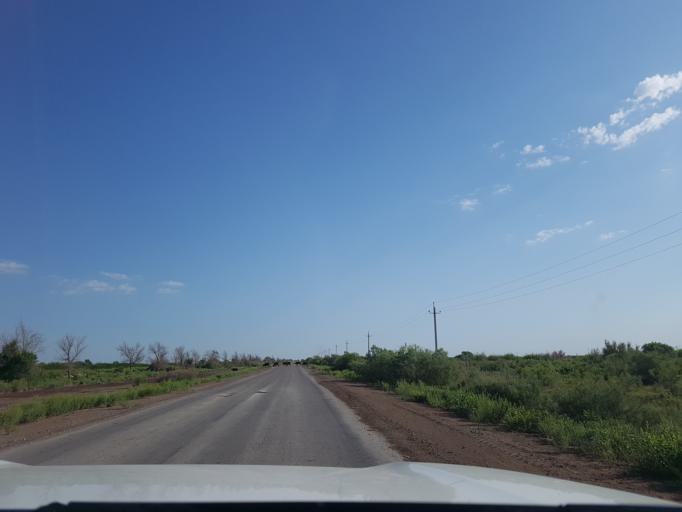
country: TM
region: Dasoguz
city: Koeneuergench
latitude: 41.8820
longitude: 58.7065
